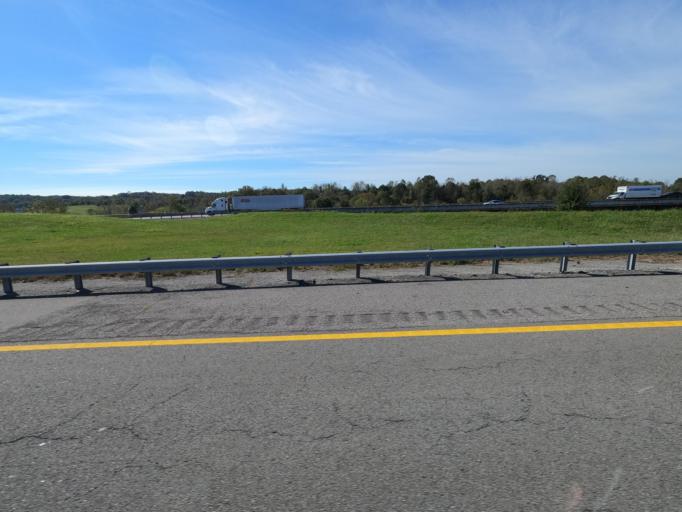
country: US
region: Tennessee
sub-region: Dickson County
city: Burns
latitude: 36.0217
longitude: -87.2641
